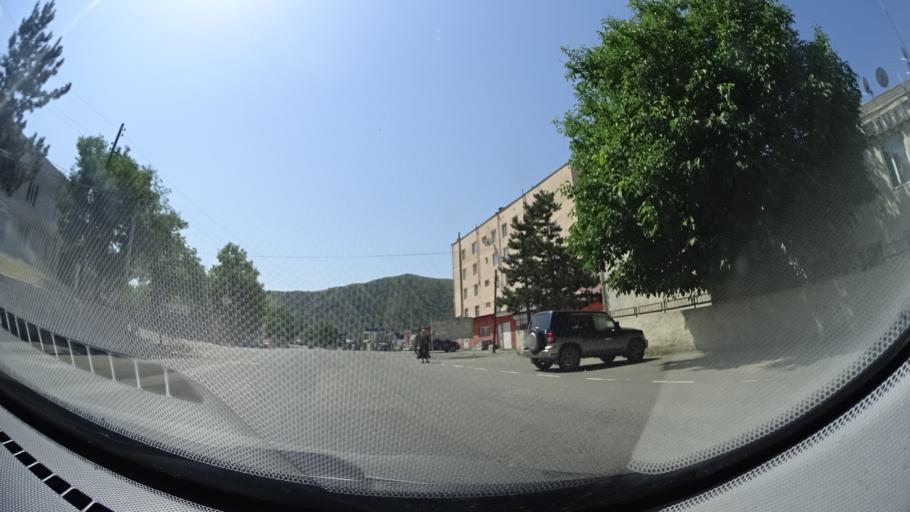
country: GE
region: Samtskhe-Javakheti
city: Aspindza
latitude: 41.5690
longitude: 43.2551
